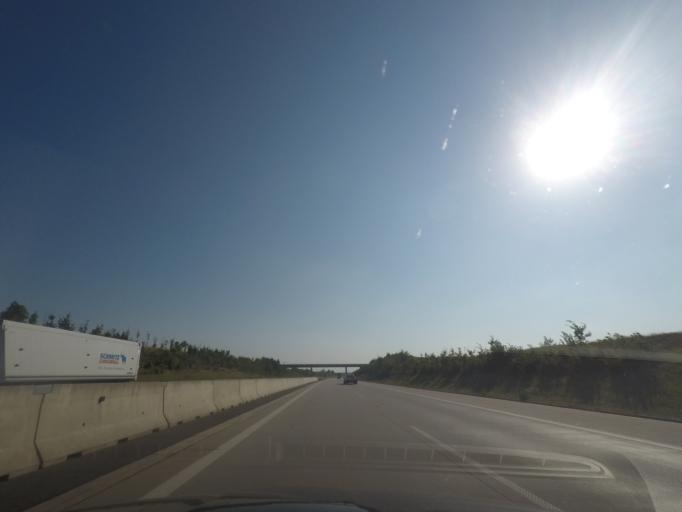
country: CZ
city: Bilovec
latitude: 49.7069
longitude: 17.9925
